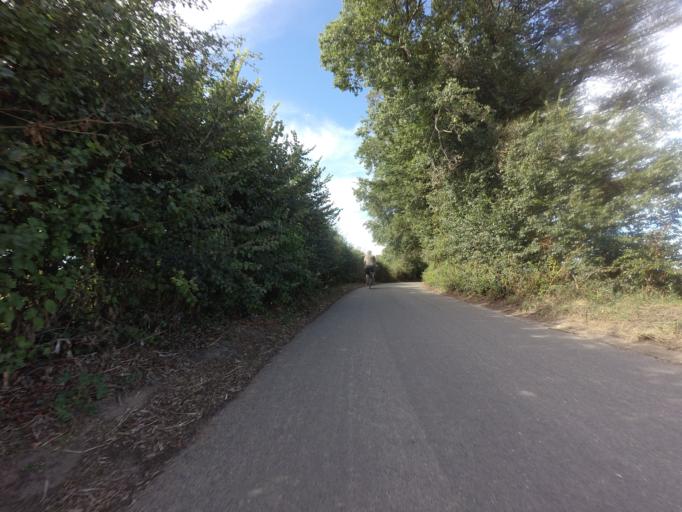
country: GB
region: England
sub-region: Kent
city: Herne Bay
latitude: 51.3705
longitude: 1.1854
